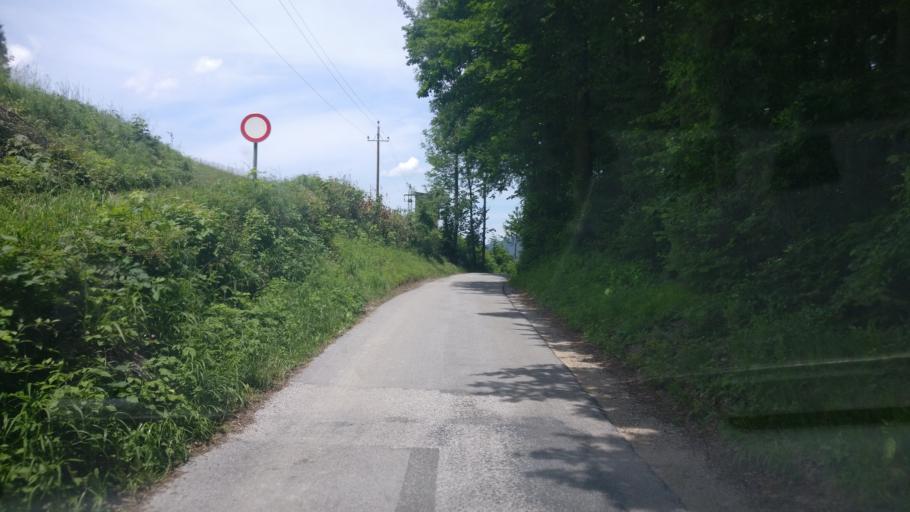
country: AT
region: Salzburg
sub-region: Politischer Bezirk Hallein
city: Hallein
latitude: 47.6600
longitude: 13.1150
